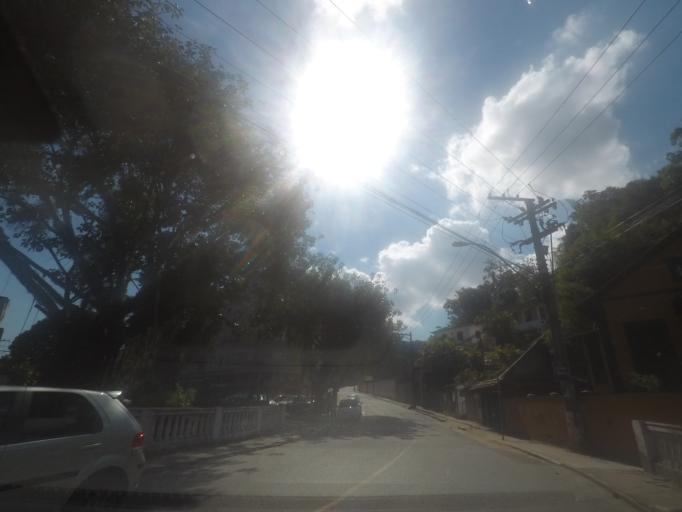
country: BR
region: Rio de Janeiro
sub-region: Petropolis
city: Petropolis
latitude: -22.5207
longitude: -43.1885
